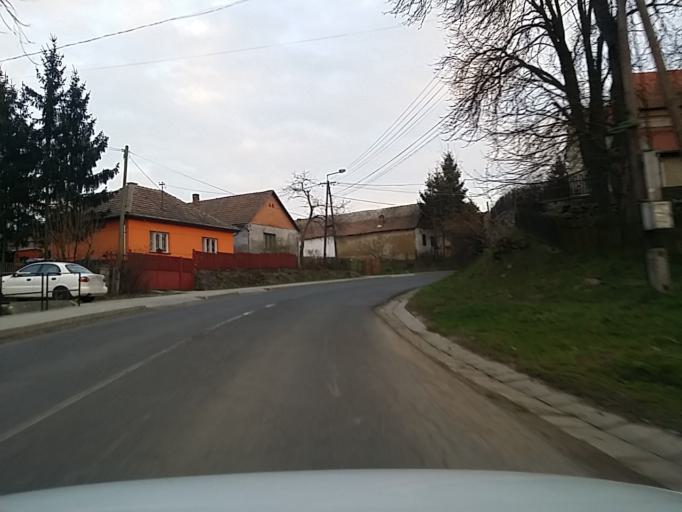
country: HU
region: Nograd
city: Batonyterenye
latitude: 47.9910
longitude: 19.8419
